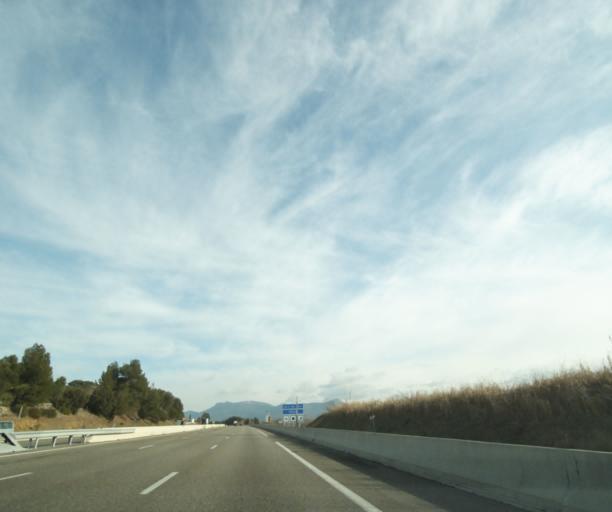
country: FR
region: Provence-Alpes-Cote d'Azur
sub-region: Departement des Bouches-du-Rhone
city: Rousset
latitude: 43.4718
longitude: 5.6382
